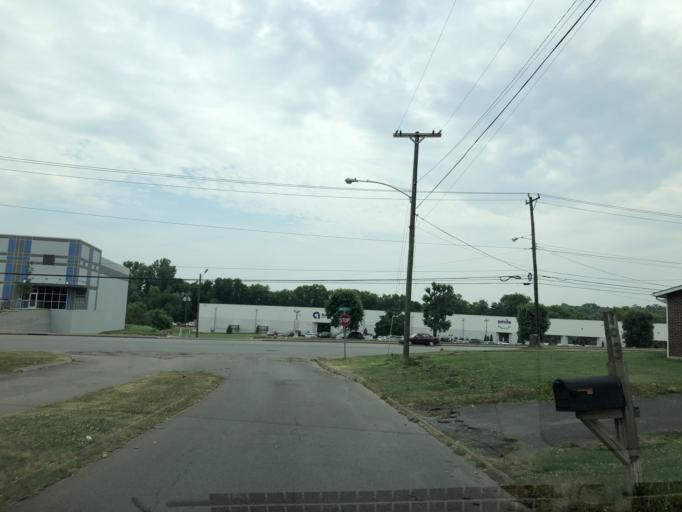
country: US
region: Tennessee
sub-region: Davidson County
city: Oak Hill
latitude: 36.0787
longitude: -86.6846
